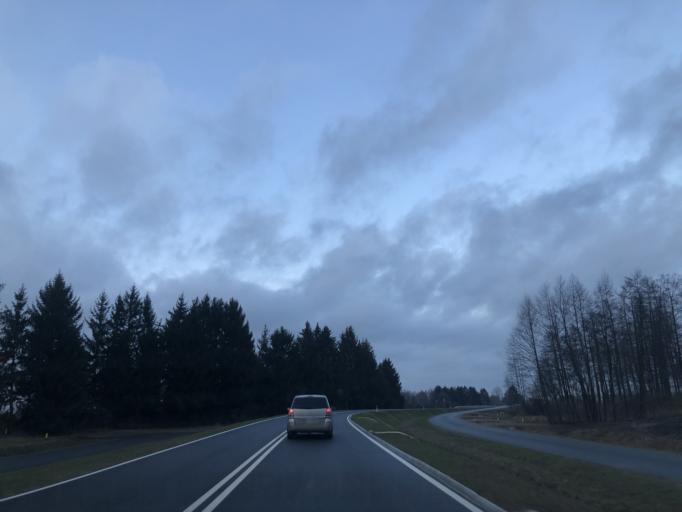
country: PL
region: Podlasie
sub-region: Lomza
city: Lomza
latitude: 53.1273
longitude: 22.0484
